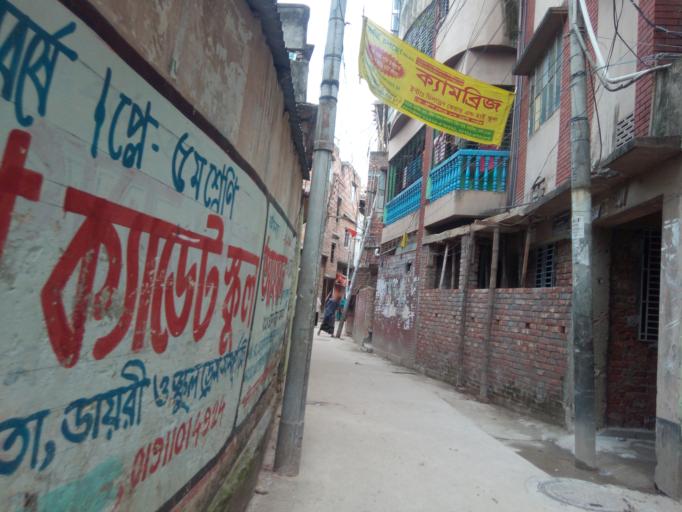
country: BD
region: Dhaka
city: Azimpur
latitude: 23.7280
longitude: 90.3725
